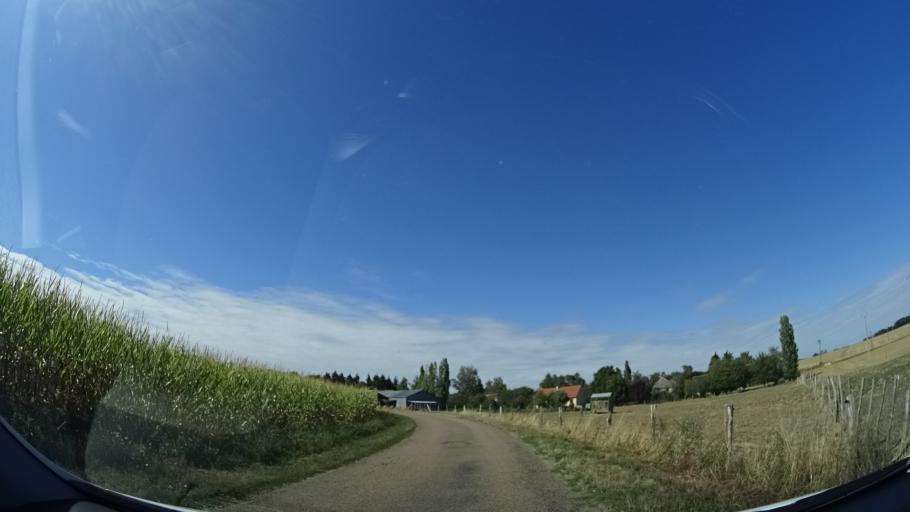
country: FR
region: Centre
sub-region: Departement du Loiret
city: Trigueres
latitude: 47.9570
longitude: 2.9792
